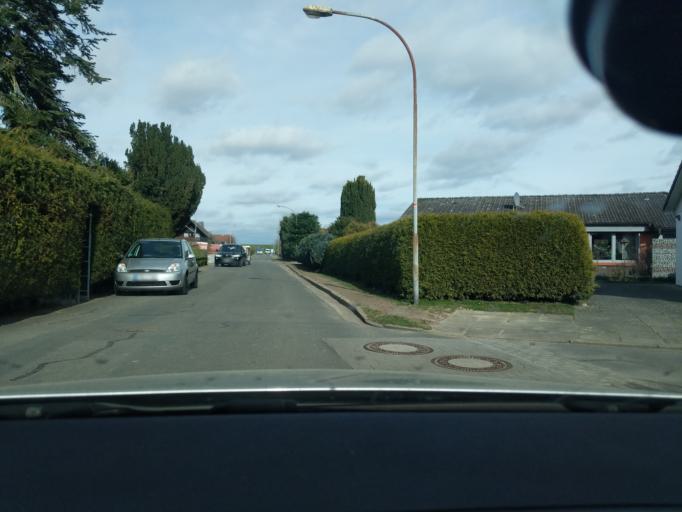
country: DE
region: Lower Saxony
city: Drochtersen
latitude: 53.7124
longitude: 9.3870
